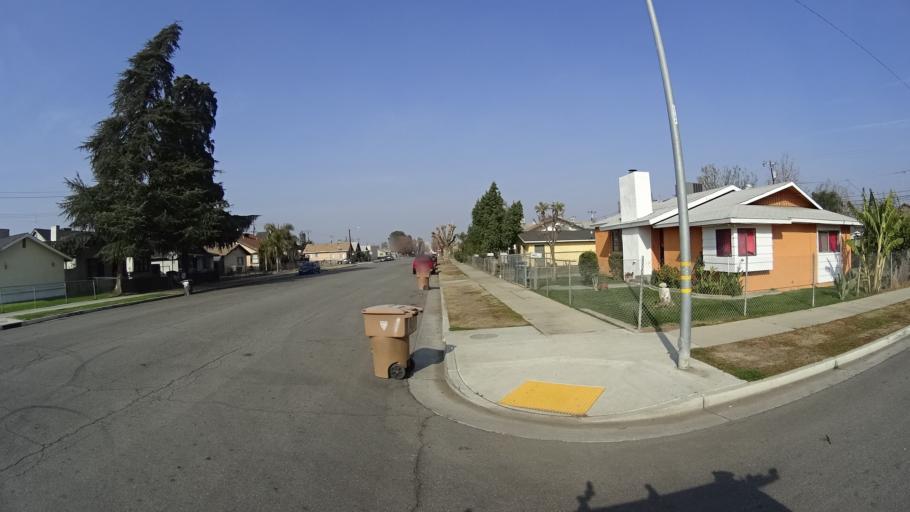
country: US
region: California
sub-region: Kern County
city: Bakersfield
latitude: 35.3617
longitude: -119.0176
